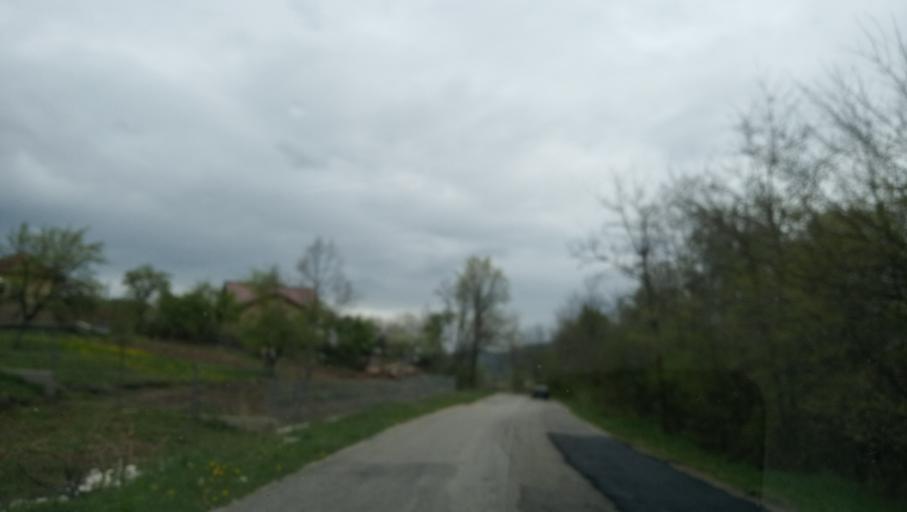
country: RO
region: Valcea
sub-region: Comuna Daesti
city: Daesti
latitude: 45.1899
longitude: 24.3854
